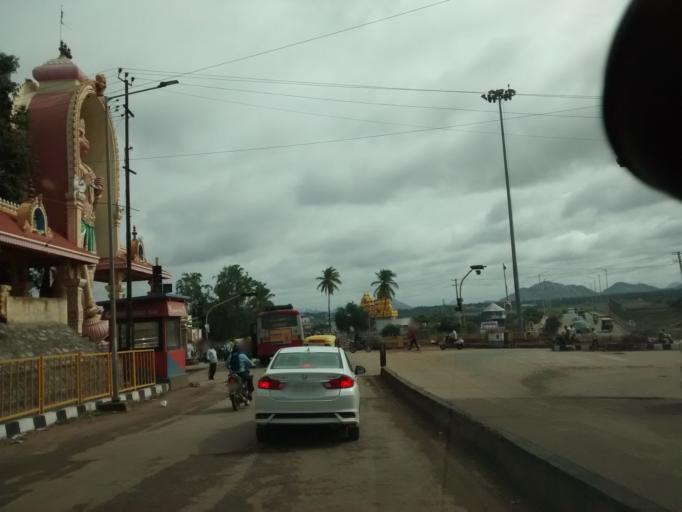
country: IN
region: Karnataka
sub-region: Tumkur
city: Tumkur
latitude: 13.3475
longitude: 77.1022
